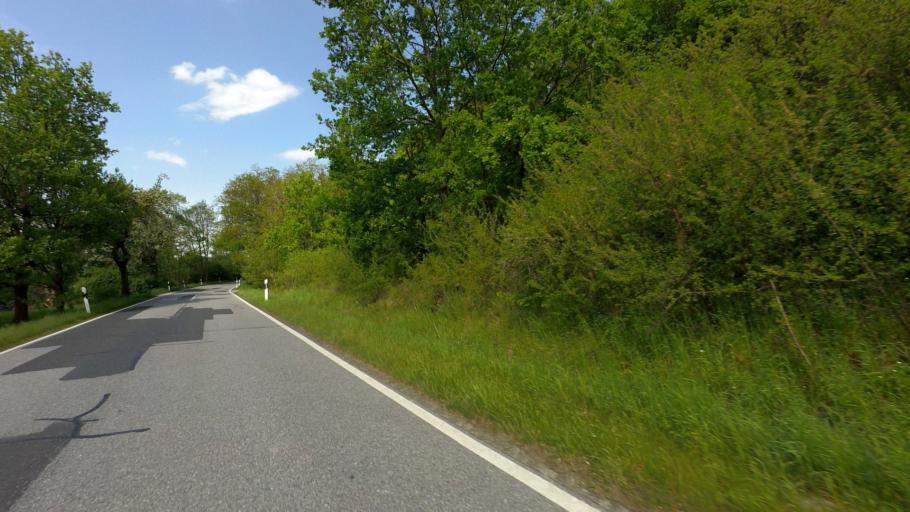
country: DE
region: Mecklenburg-Vorpommern
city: Mollenhagen
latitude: 53.5515
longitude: 12.9219
